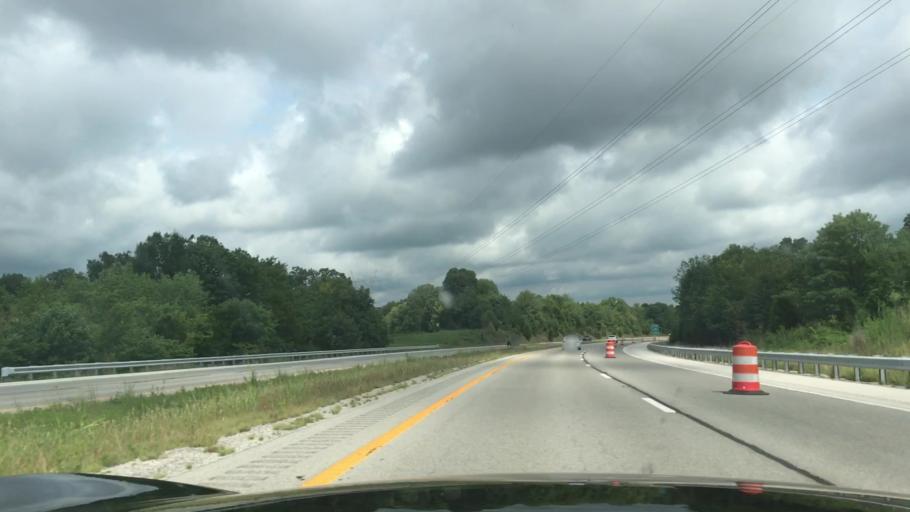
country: US
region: Kentucky
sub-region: Butler County
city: Morgantown
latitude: 37.1002
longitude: -86.6375
